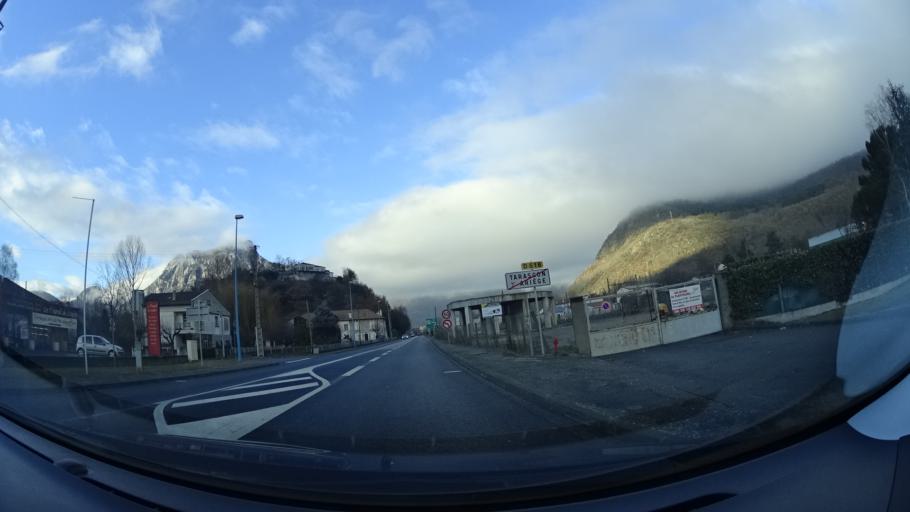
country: FR
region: Midi-Pyrenees
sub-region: Departement de l'Ariege
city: Tarascon-sur-Ariege
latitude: 42.8471
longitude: 1.6000
